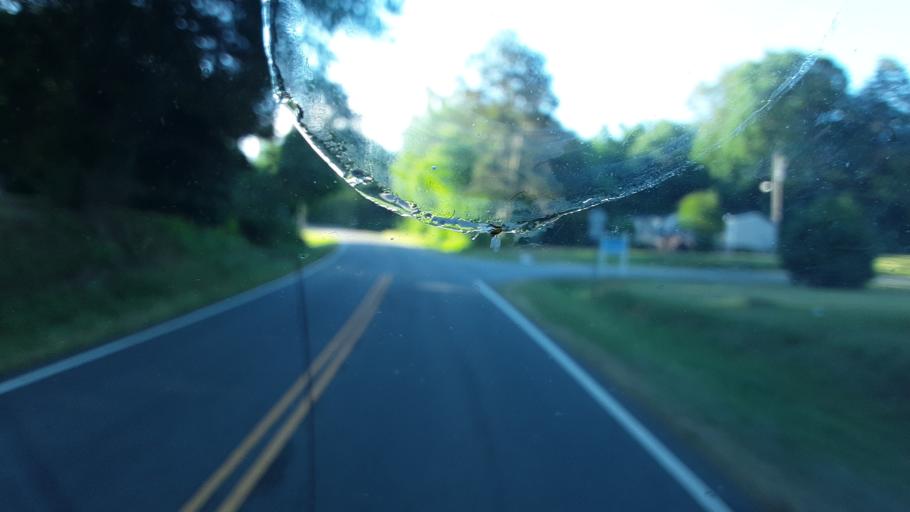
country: US
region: Virginia
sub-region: Pittsylvania County
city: Chatham
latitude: 36.8229
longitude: -79.4206
